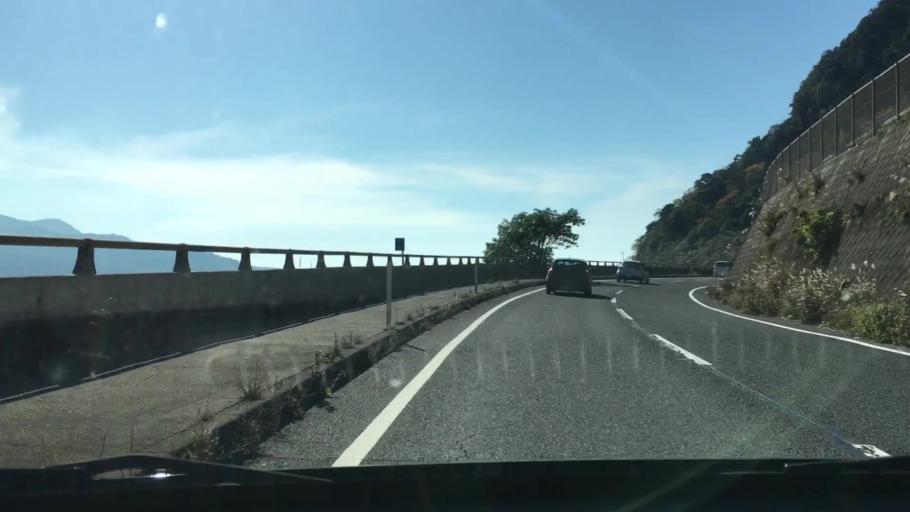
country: JP
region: Kagoshima
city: Kagoshima-shi
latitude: 31.6423
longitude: 130.6029
